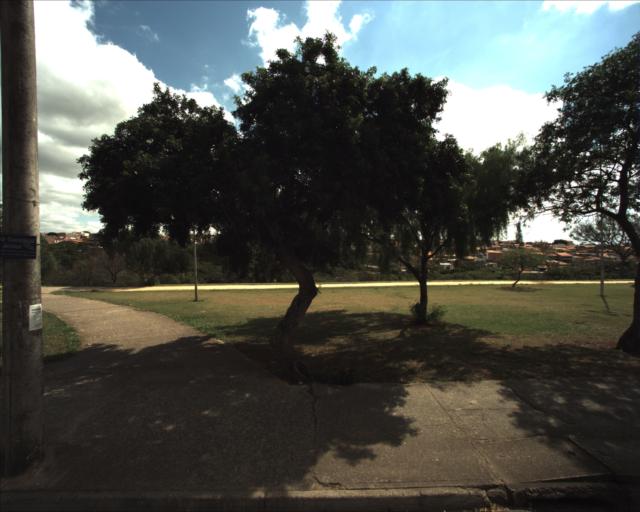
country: BR
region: Sao Paulo
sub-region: Sorocaba
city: Sorocaba
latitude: -23.5010
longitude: -47.5204
